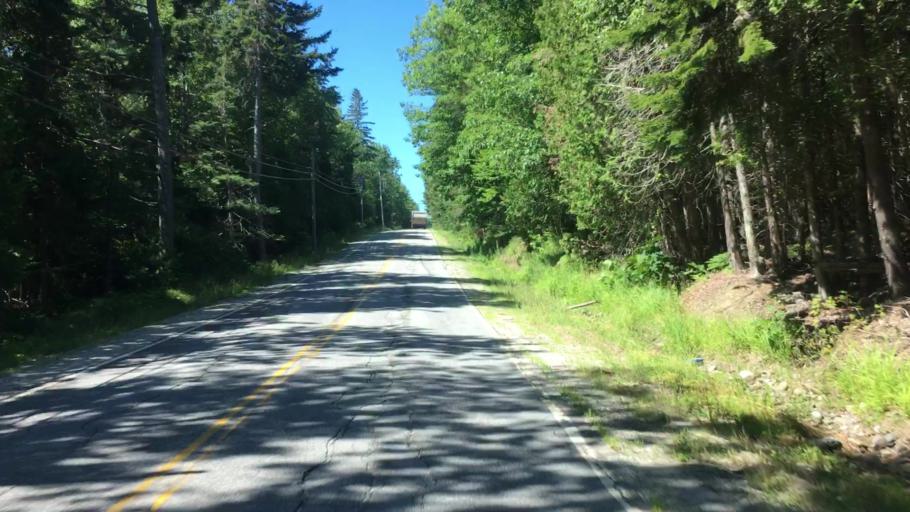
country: US
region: Maine
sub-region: Hancock County
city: Sedgwick
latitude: 44.3279
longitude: -68.6008
